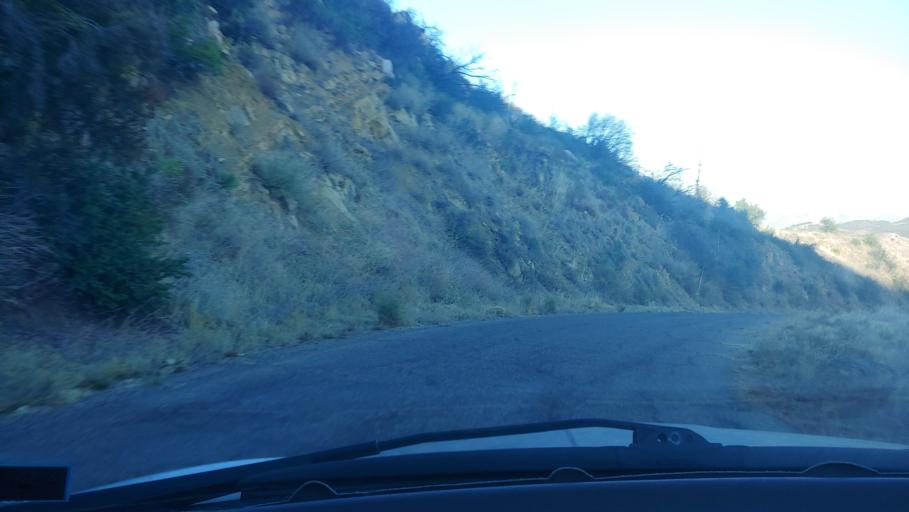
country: US
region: California
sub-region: Santa Barbara County
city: Mission Canyon
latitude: 34.5070
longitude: -119.7661
